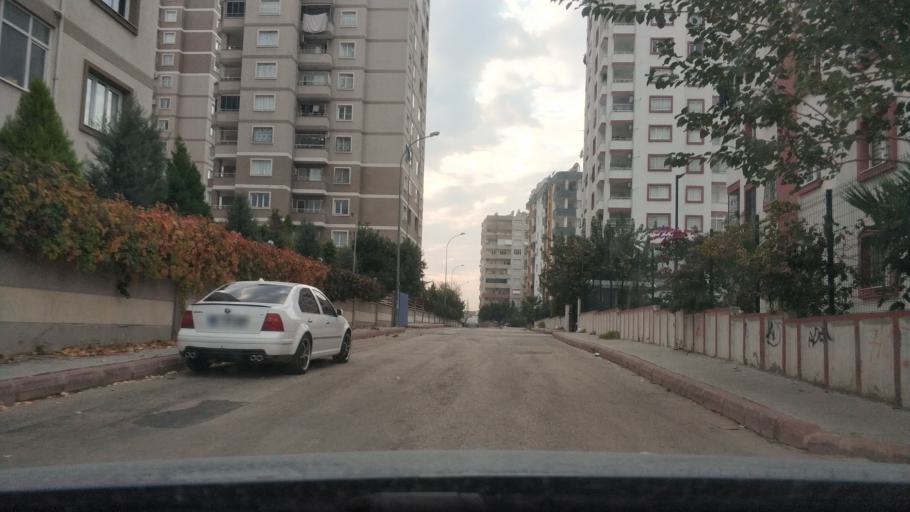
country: TR
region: Adana
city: Seyhan
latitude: 37.0159
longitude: 35.2899
